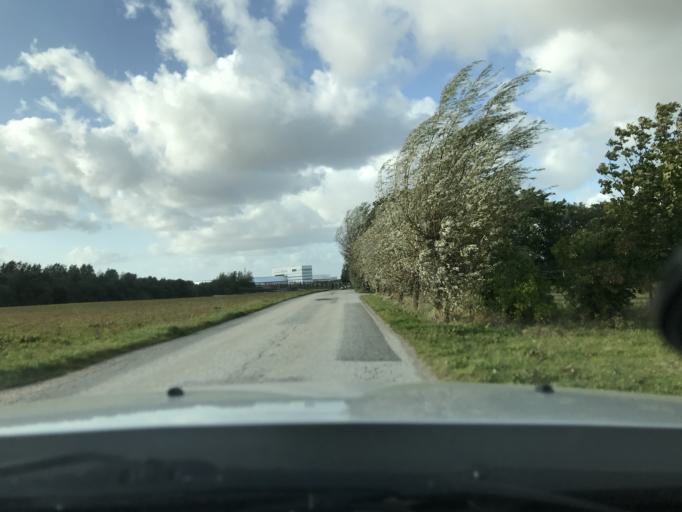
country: SE
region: Skane
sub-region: Lunds Kommun
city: Lund
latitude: 55.7210
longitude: 13.2411
